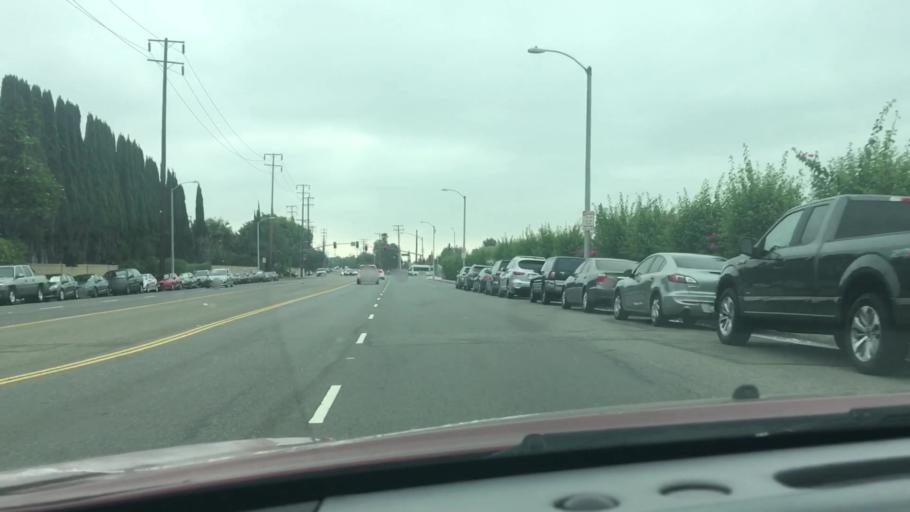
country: US
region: California
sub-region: Orange County
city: Buena Park
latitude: 33.8777
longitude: -117.9893
